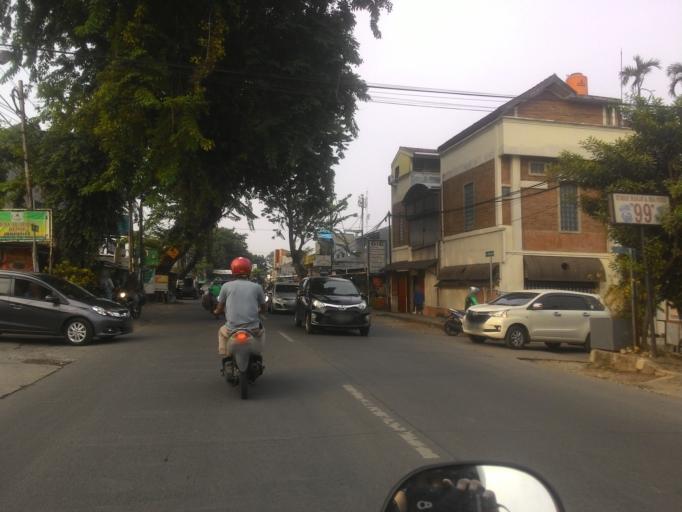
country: ID
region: West Java
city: Depok
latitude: -6.3939
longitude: 106.8370
